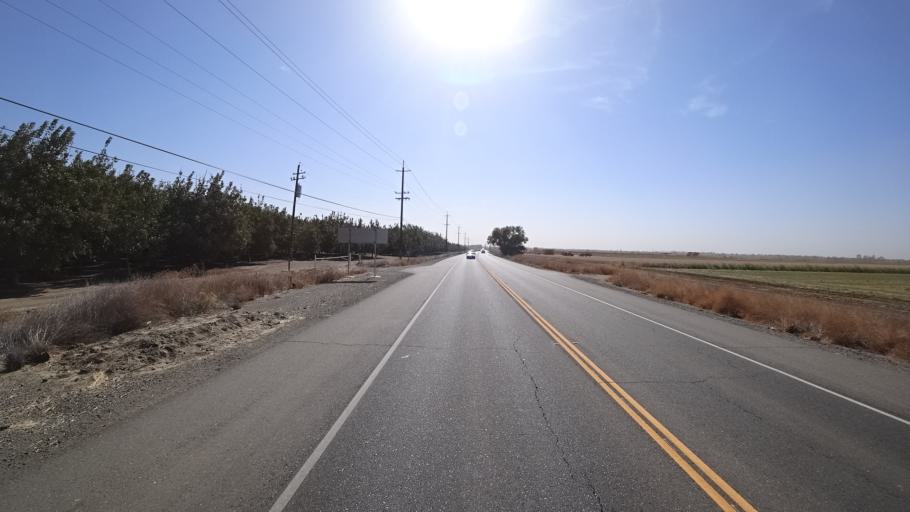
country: US
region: California
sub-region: Yolo County
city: Davis
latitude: 38.5872
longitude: -121.7303
